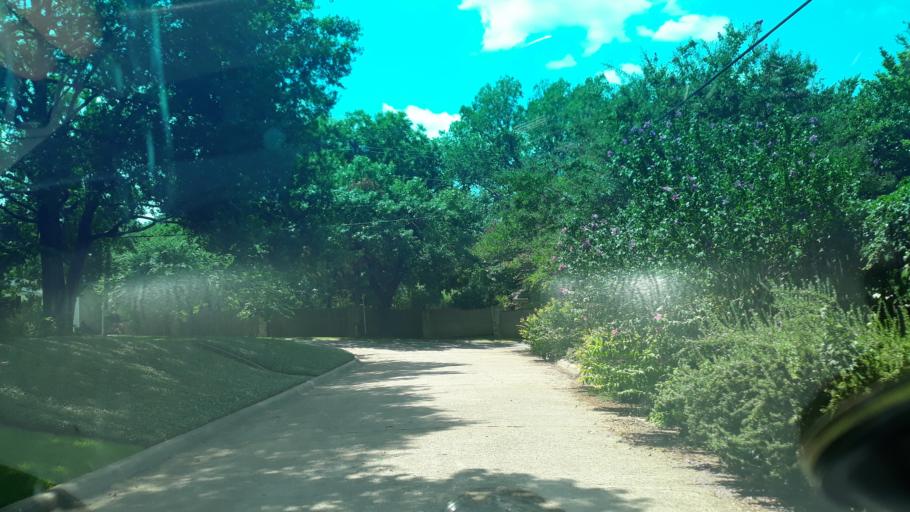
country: US
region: Texas
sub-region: Dallas County
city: Highland Park
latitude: 32.8245
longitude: -96.7338
